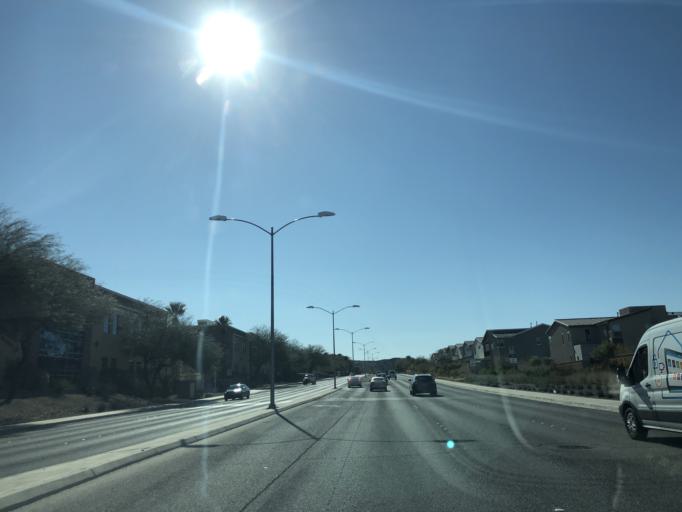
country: US
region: Nevada
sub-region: Clark County
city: Whitney
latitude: 36.0147
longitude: -115.0585
